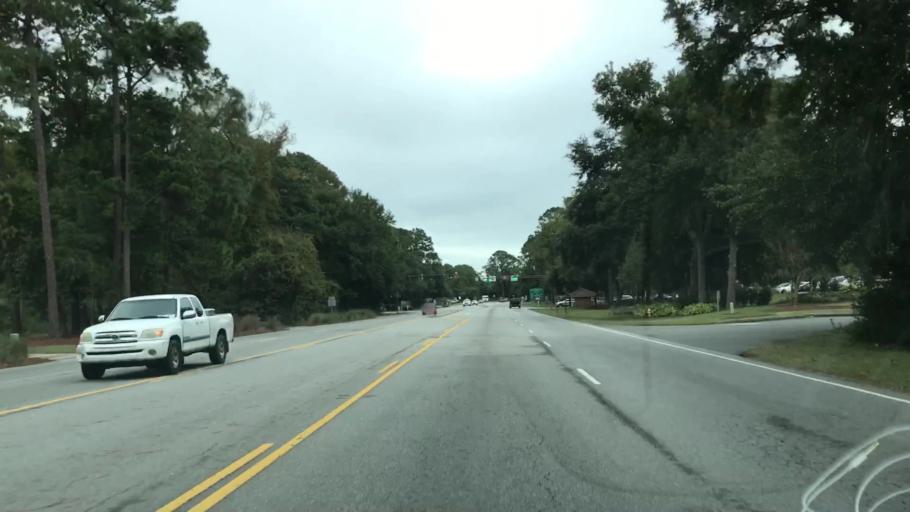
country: US
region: South Carolina
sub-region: Beaufort County
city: Hilton Head Island
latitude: 32.1590
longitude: -80.7656
